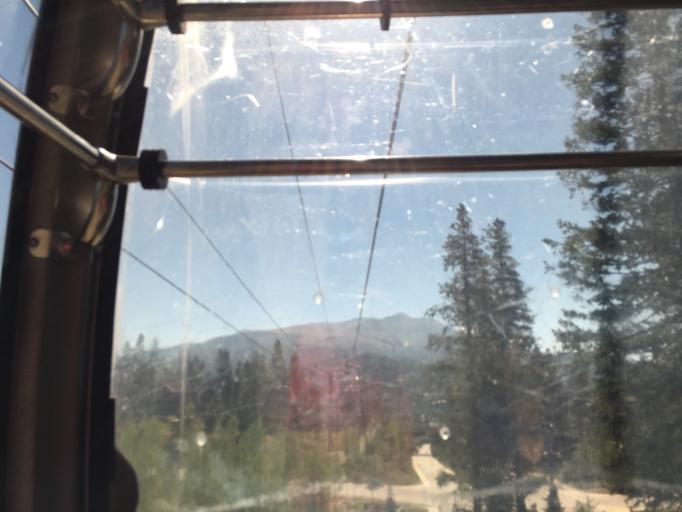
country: US
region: Colorado
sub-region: Summit County
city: Breckenridge
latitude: 39.4880
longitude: -106.0540
